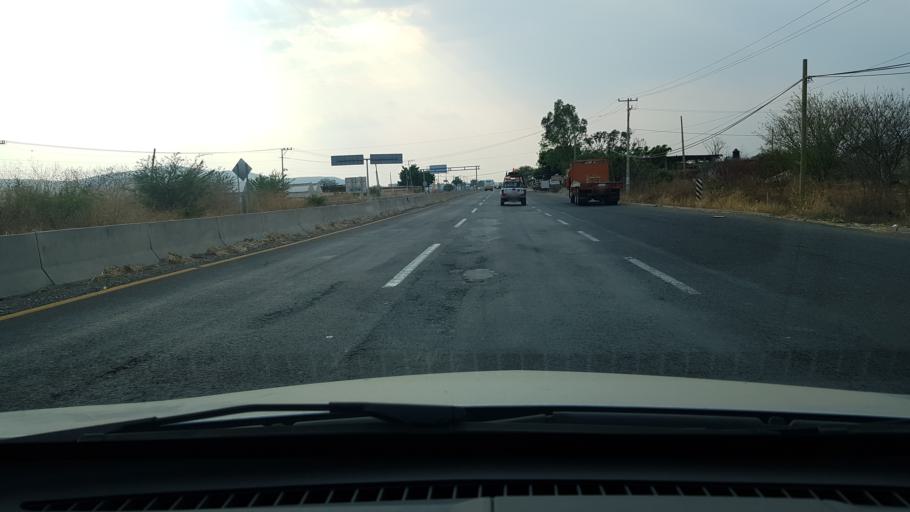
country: MX
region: Morelos
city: Amayuca
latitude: 18.7319
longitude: -98.8135
